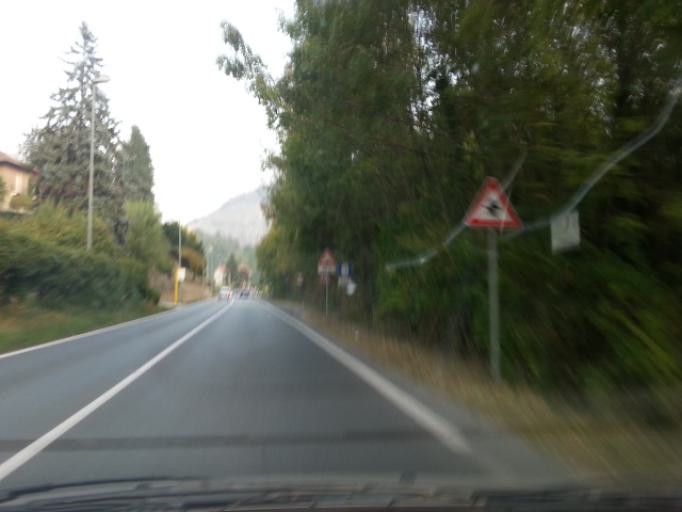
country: IT
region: Piedmont
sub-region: Provincia di Torino
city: Trana
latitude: 45.0355
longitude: 7.4009
